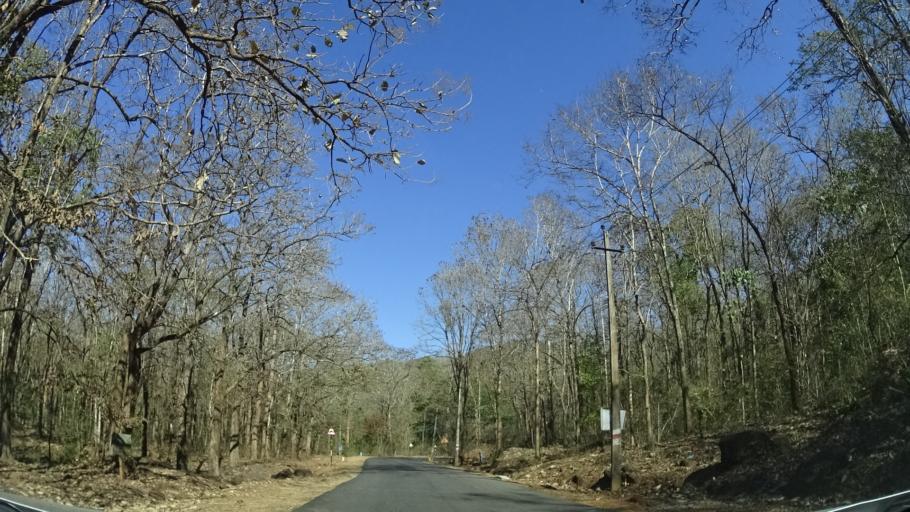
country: IN
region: Karnataka
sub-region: Chikmagalur
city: Koppa
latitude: 13.3538
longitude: 75.4957
